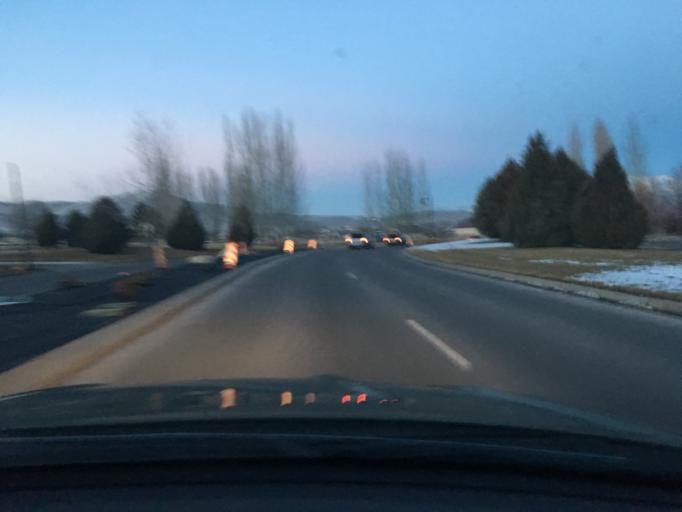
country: US
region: Utah
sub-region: Utah County
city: Eagle Mountain
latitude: 40.3612
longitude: -111.9853
